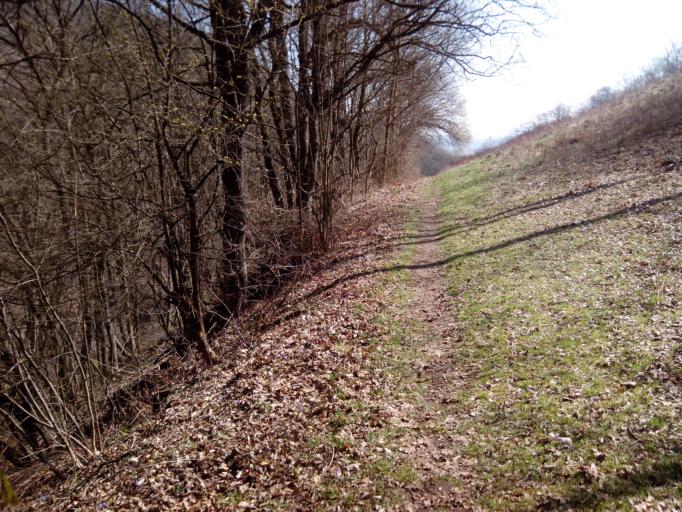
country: CZ
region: Central Bohemia
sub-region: Okres Beroun
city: Beroun
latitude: 49.9327
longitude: 14.1205
